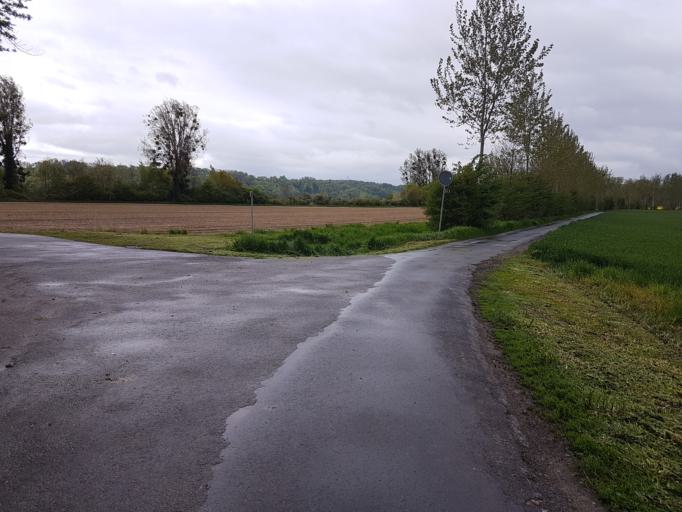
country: CH
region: Vaud
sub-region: Jura-Nord vaudois District
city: Yverdon-les-Bains
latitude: 46.7645
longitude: 6.6219
